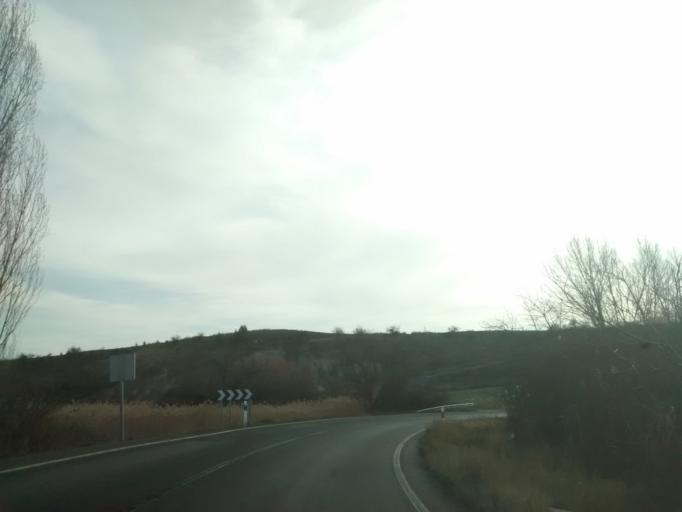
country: ES
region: Aragon
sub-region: Provincia de Huesca
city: Bailo
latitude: 42.5902
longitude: -0.8364
